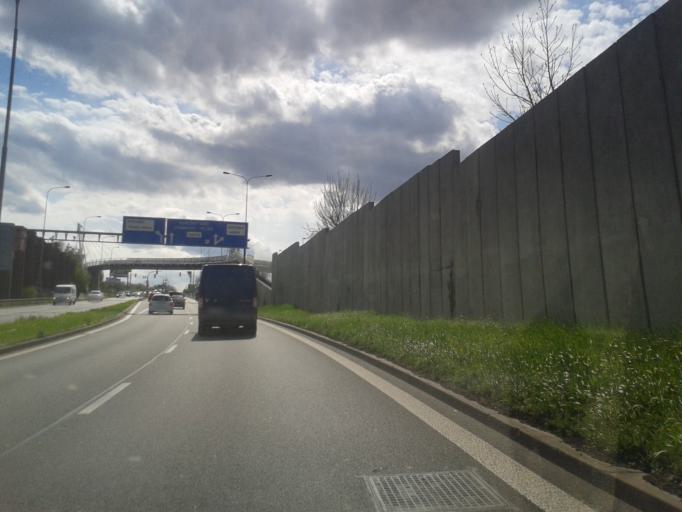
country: CZ
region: Praha
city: Branik
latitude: 50.0354
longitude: 14.3840
